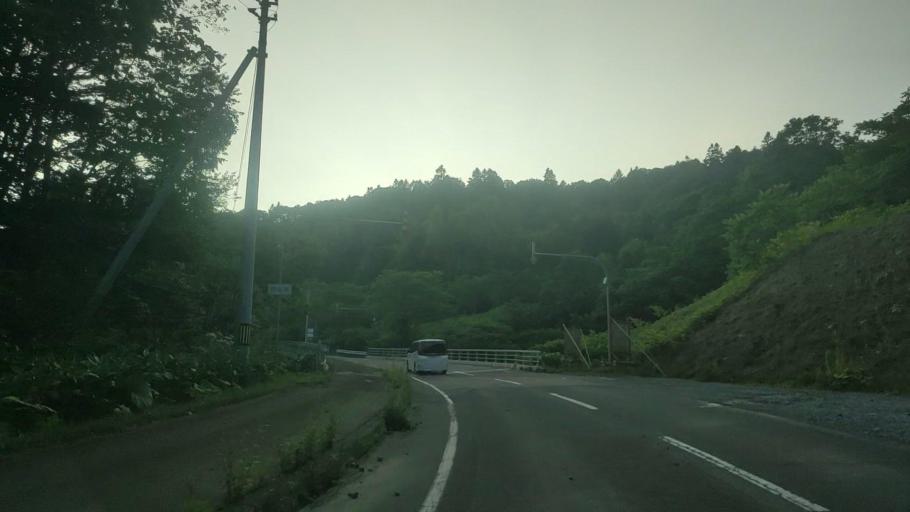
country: JP
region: Hokkaido
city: Bibai
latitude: 43.2378
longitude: 142.0360
